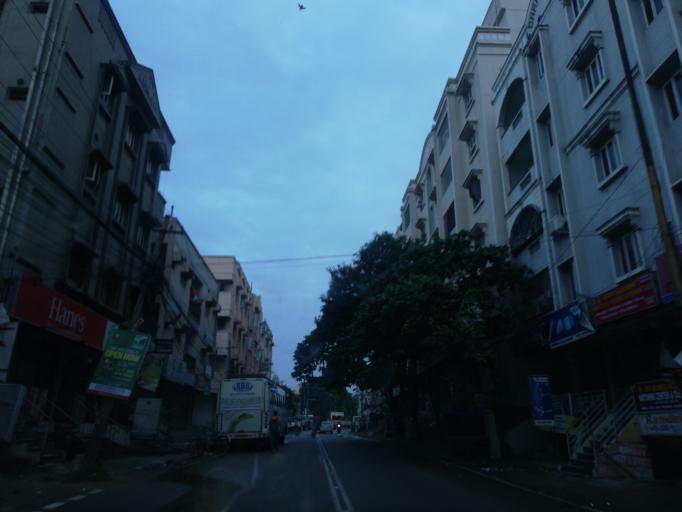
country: IN
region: Telangana
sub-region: Rangareddi
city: Kukatpalli
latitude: 17.4866
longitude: 78.3948
